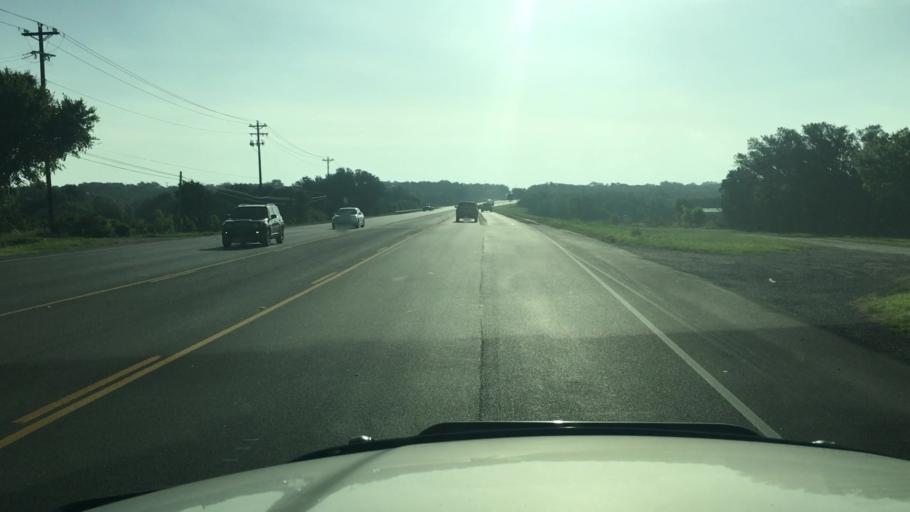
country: US
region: Texas
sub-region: Hays County
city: Dripping Springs
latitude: 30.2053
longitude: -98.1481
